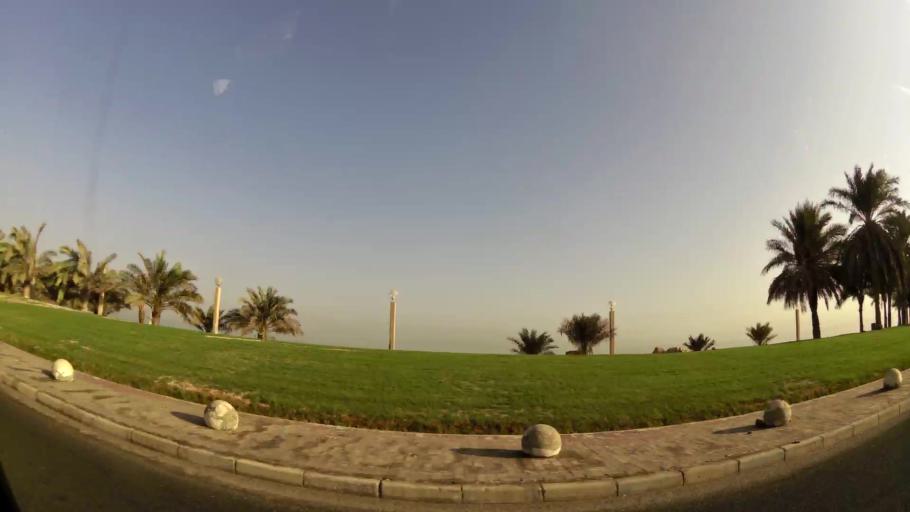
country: KW
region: Al Asimah
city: Ad Dasmah
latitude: 29.3680
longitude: 48.0175
